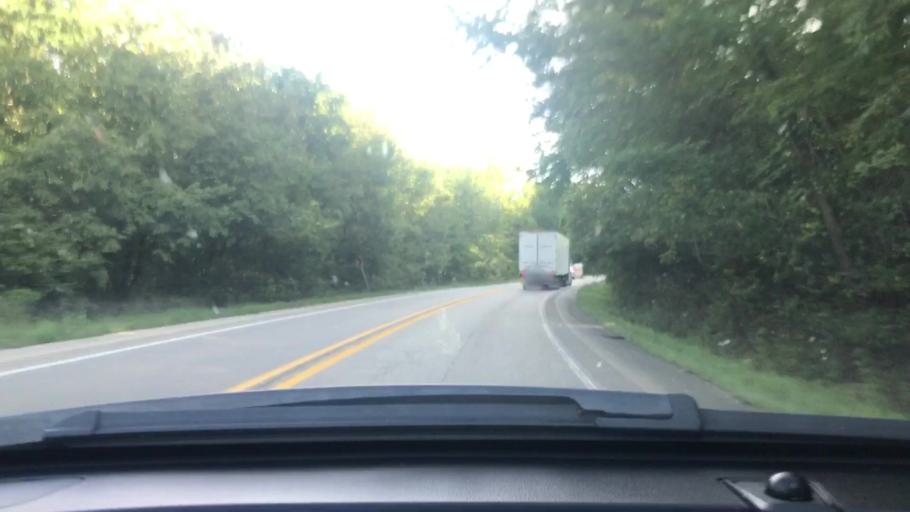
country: US
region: Arkansas
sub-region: Randolph County
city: Pocahontas
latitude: 36.2166
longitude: -91.2164
